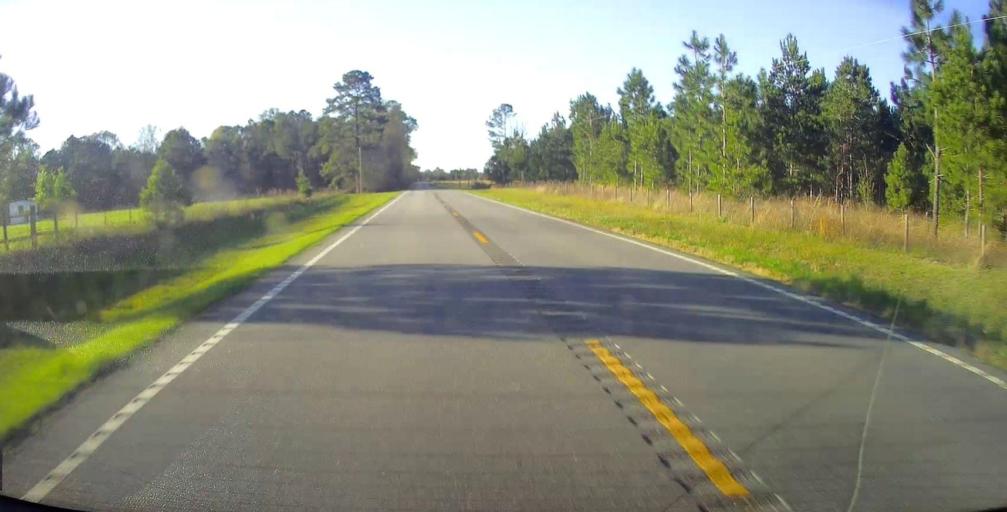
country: US
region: Georgia
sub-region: Pulaski County
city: Hawkinsville
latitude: 32.2268
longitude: -83.3927
